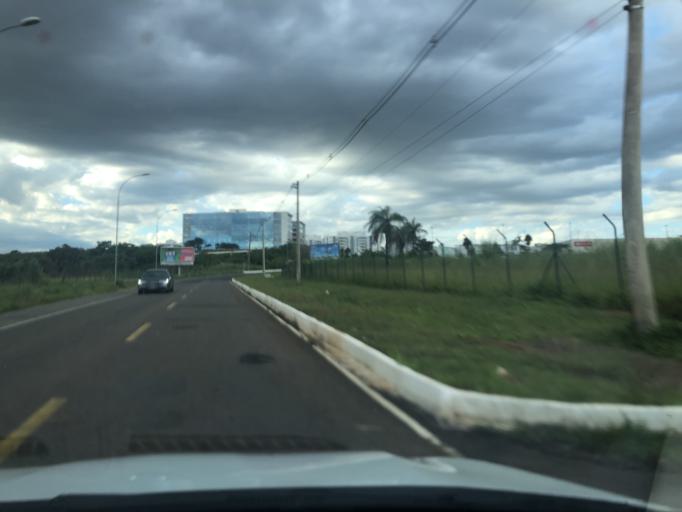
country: BR
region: Federal District
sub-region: Brasilia
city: Brasilia
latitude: -15.8359
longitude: -47.9580
